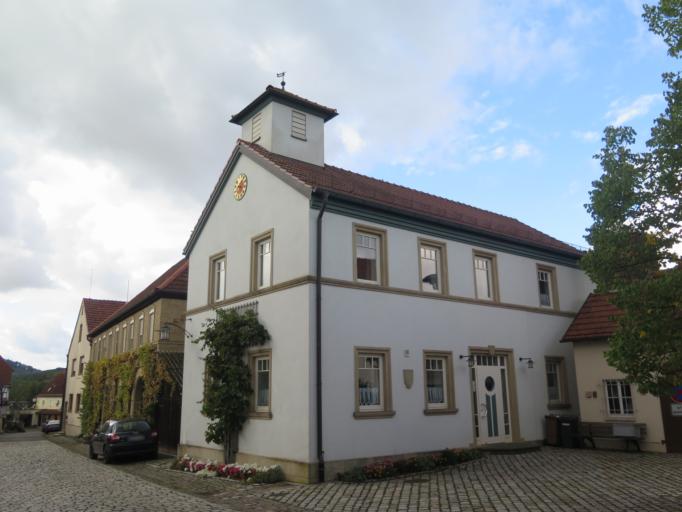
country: DE
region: Bavaria
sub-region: Regierungsbezirk Unterfranken
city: Zeil
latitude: 50.0522
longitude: 10.5906
